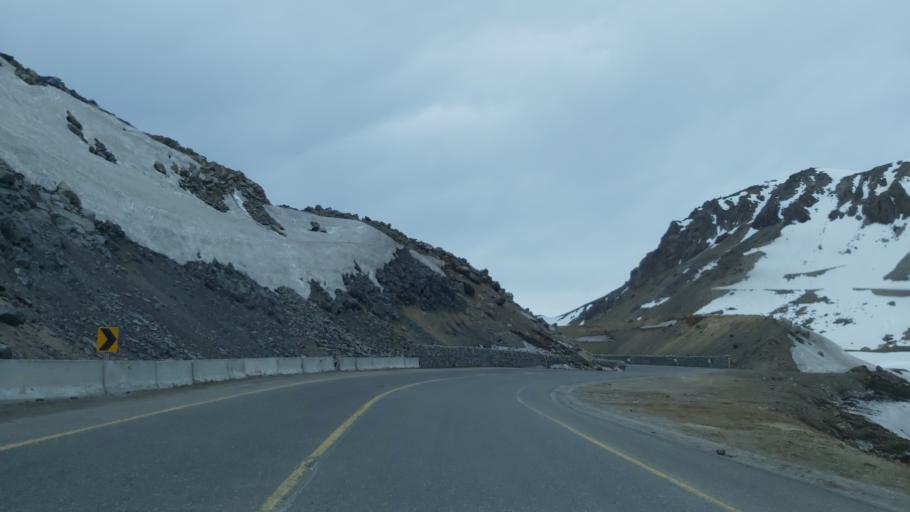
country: CL
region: Maule
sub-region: Provincia de Linares
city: Colbun
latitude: -36.0047
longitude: -70.5584
